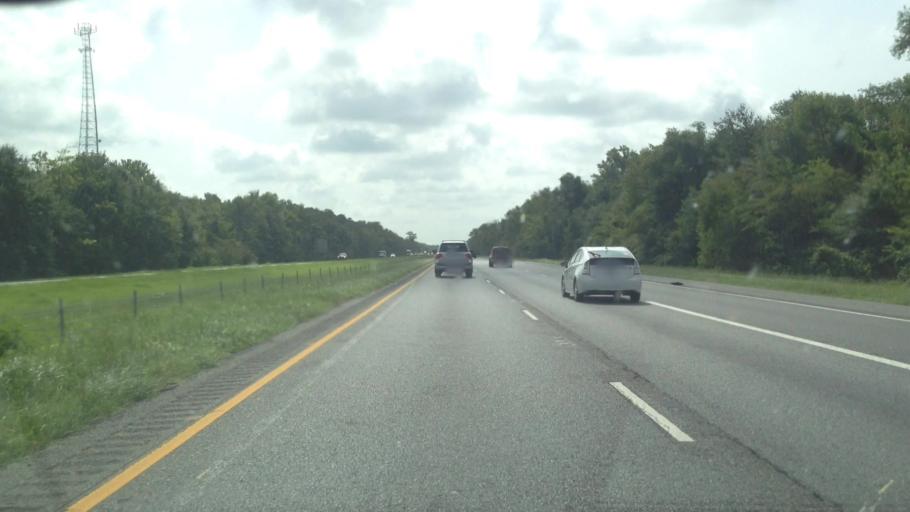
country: US
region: Louisiana
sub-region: Ascension Parish
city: Sorrento
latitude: 30.1527
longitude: -90.8012
